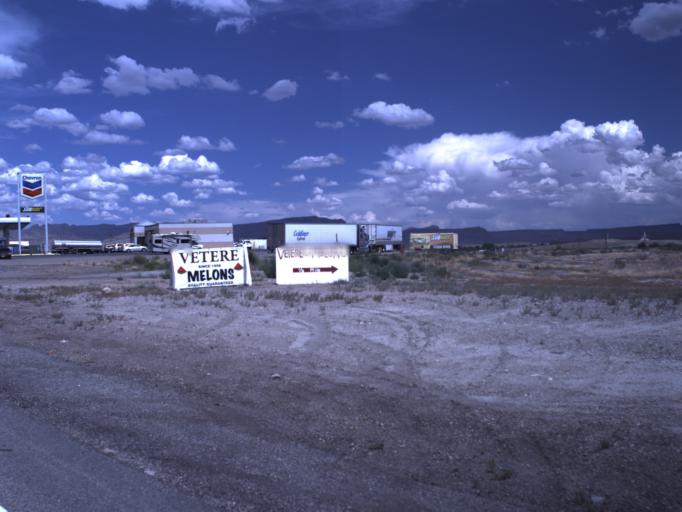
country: US
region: Utah
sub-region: Carbon County
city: East Carbon City
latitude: 38.9938
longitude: -110.1858
